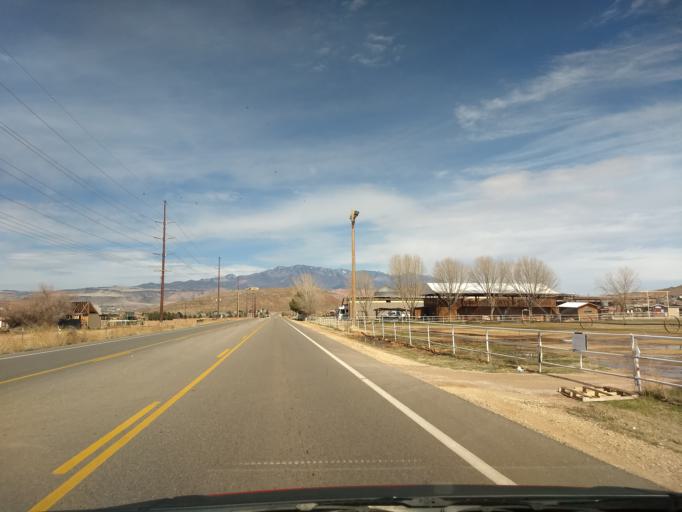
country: US
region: Utah
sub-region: Washington County
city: Washington
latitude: 37.0836
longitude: -113.4996
